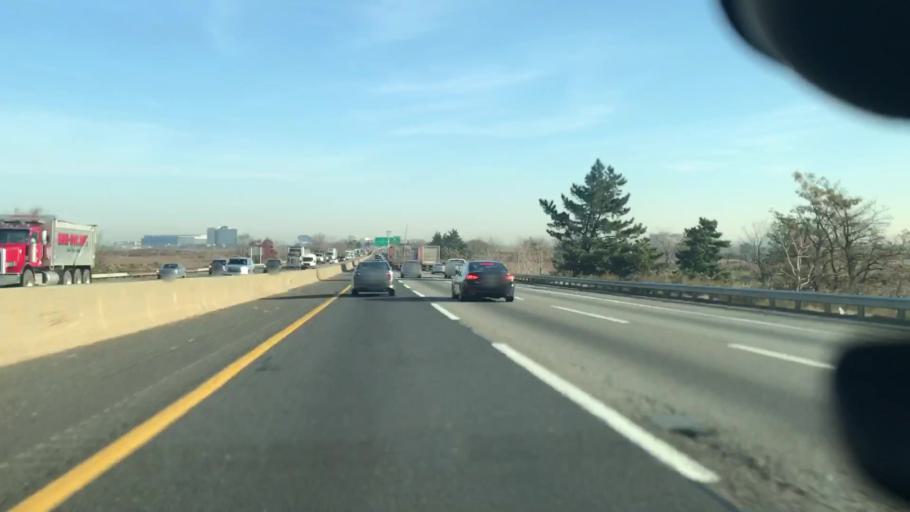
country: US
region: New Jersey
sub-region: Hudson County
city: Secaucus
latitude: 40.7851
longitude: -74.0929
